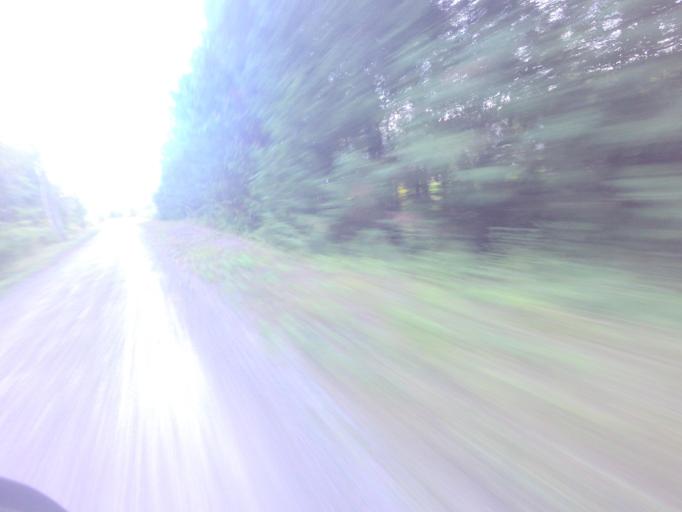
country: CA
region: Ontario
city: Bradford West Gwillimbury
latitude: 43.9971
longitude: -79.8039
